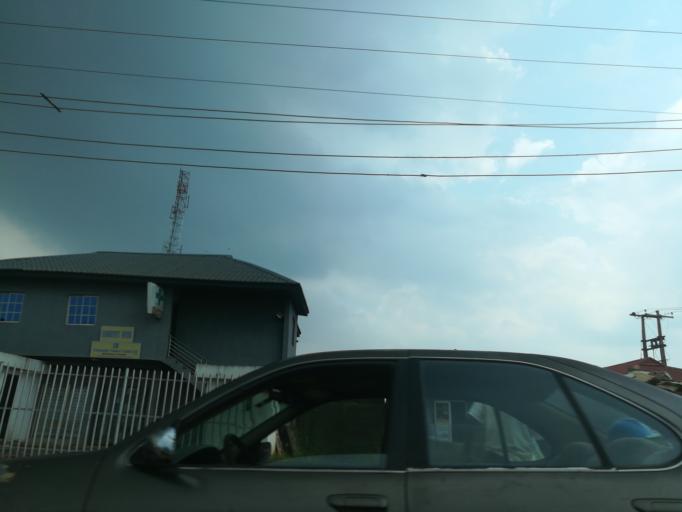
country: NG
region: Lagos
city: Ikorodu
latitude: 6.5950
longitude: 3.5888
